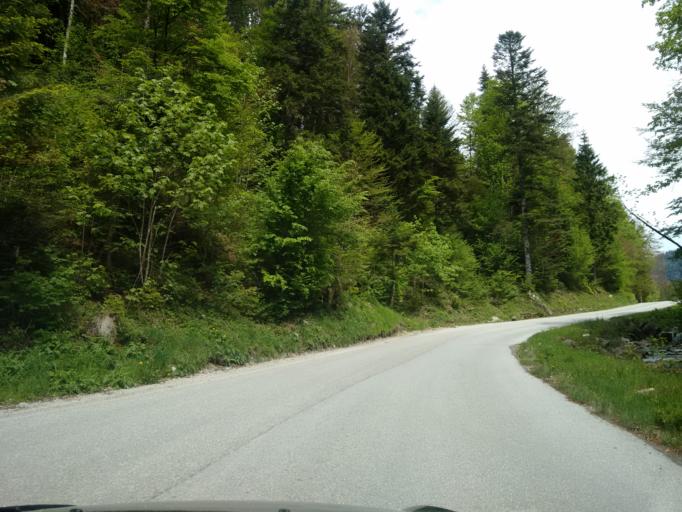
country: AT
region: Styria
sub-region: Politischer Bezirk Liezen
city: Altaussee
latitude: 47.6579
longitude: 13.7436
